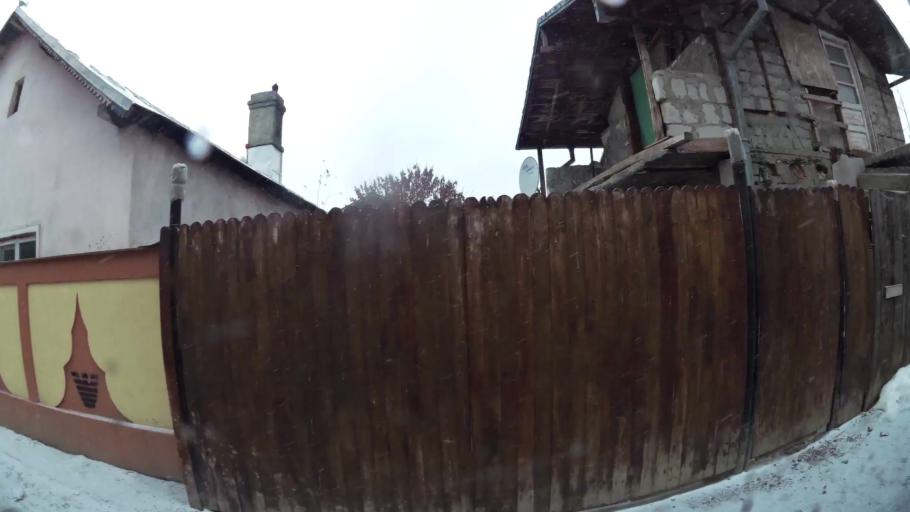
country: RO
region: Dambovita
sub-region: Municipiul Targoviste
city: Targoviste
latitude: 44.9294
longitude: 25.4325
